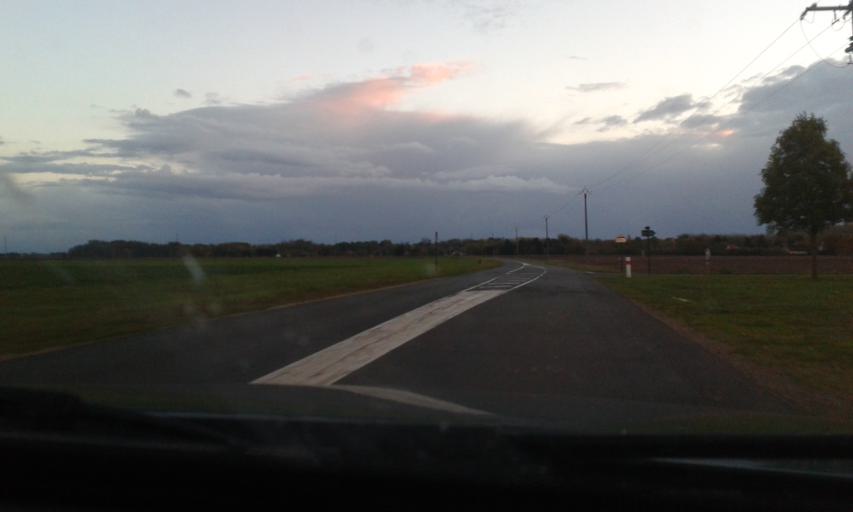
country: FR
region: Centre
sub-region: Departement du Loiret
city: Huisseau-sur-Mauves
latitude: 47.8726
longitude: 1.6957
